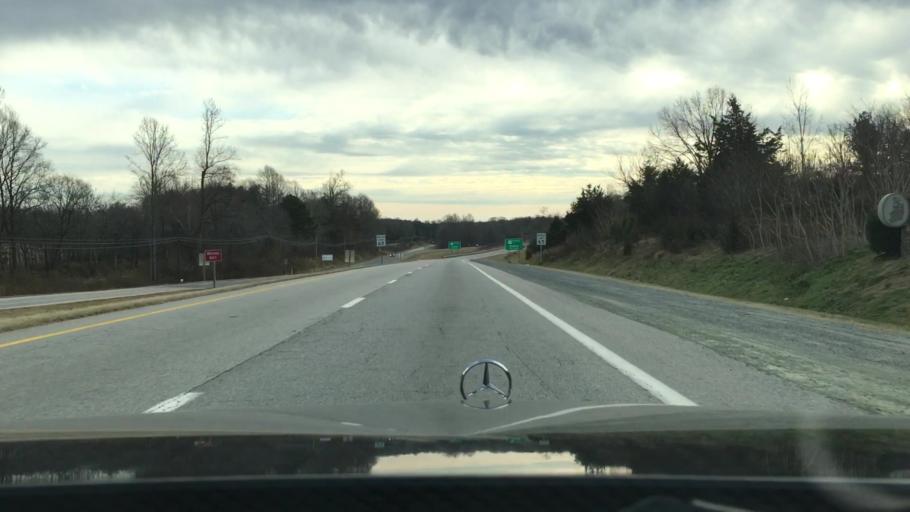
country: US
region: Virginia
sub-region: Pittsylvania County
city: Gretna
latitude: 36.9839
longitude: -79.3547
